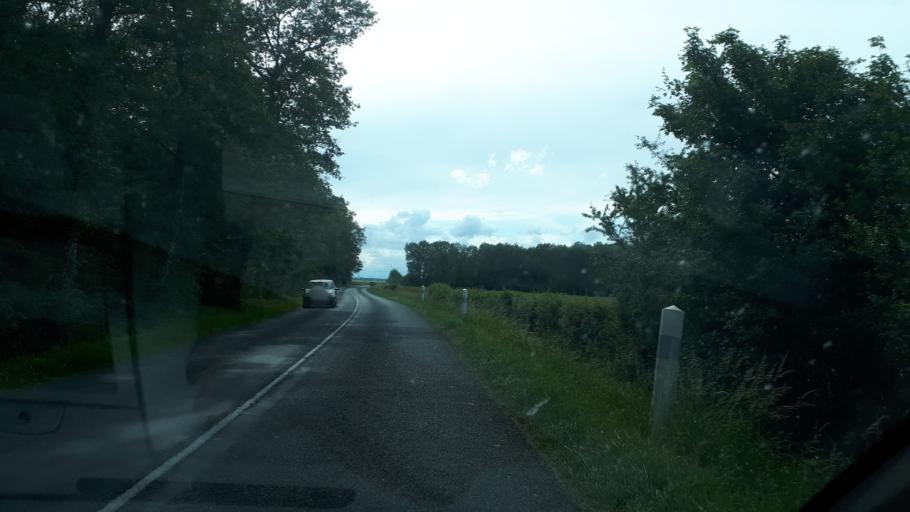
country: FR
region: Centre
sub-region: Departement du Cher
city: Marmagne
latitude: 47.0792
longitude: 2.2882
